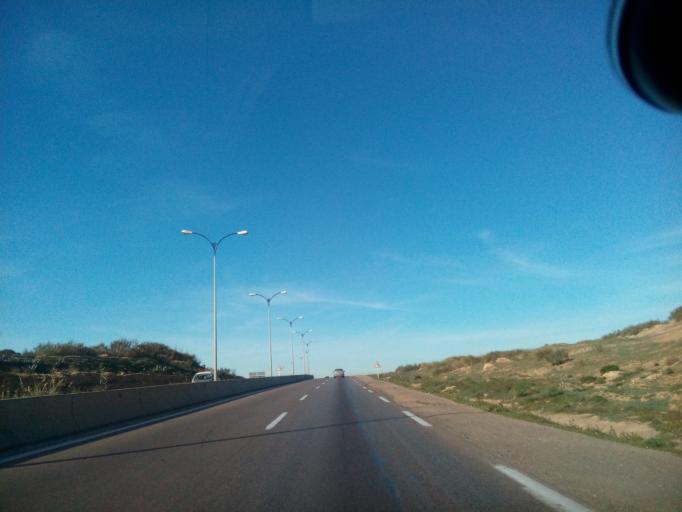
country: DZ
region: Oran
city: Ain el Bya
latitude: 35.7868
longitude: -0.1097
